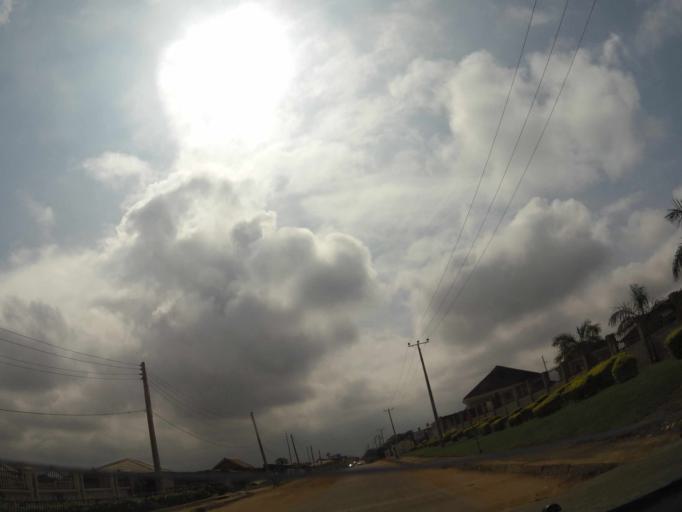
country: NG
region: Oyo
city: Ibadan
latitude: 7.4391
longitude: 3.9605
